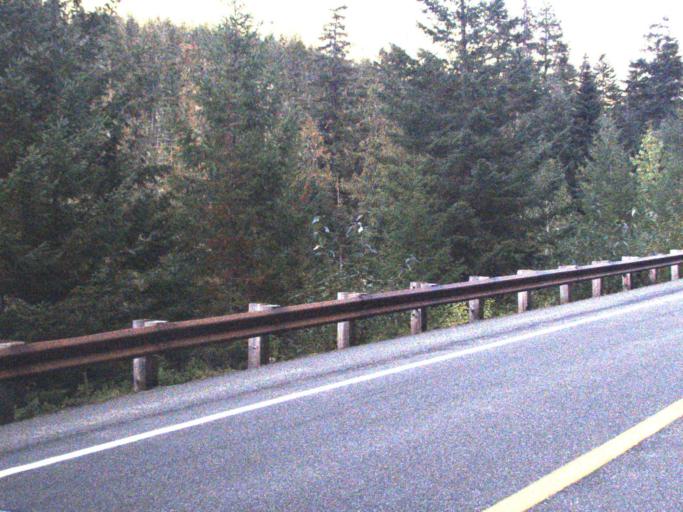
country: US
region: Washington
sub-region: Snohomish County
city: Darrington
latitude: 48.6656
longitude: -120.8725
